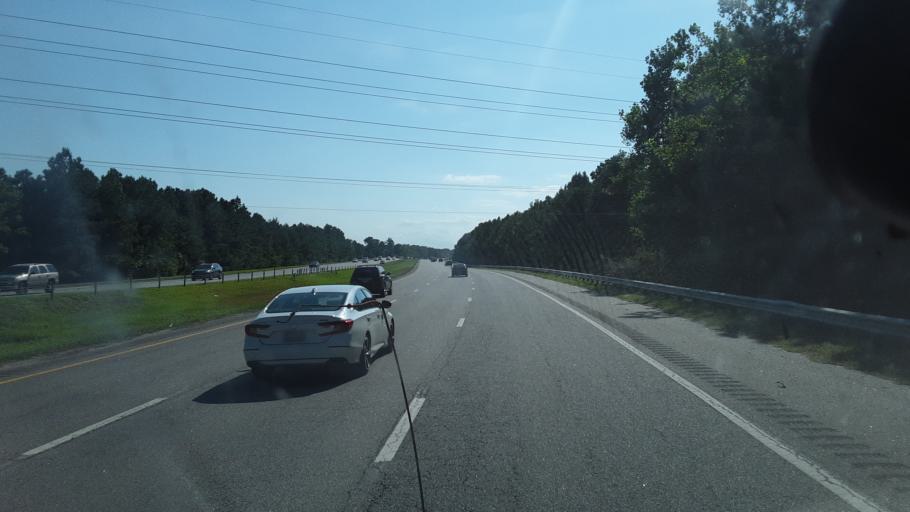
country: US
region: South Carolina
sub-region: Horry County
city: Myrtle Beach
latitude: 33.7658
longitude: -78.8337
